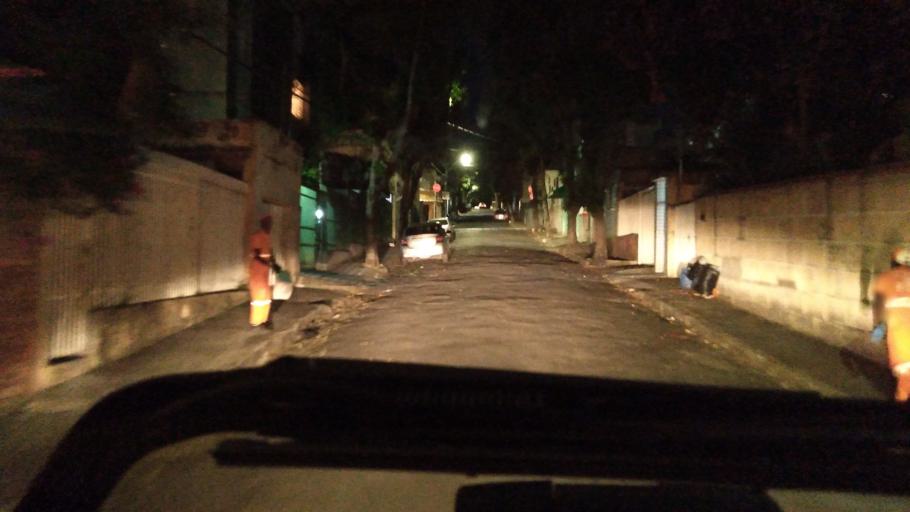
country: BR
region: Minas Gerais
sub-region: Belo Horizonte
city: Belo Horizonte
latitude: -19.9205
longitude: -43.9788
